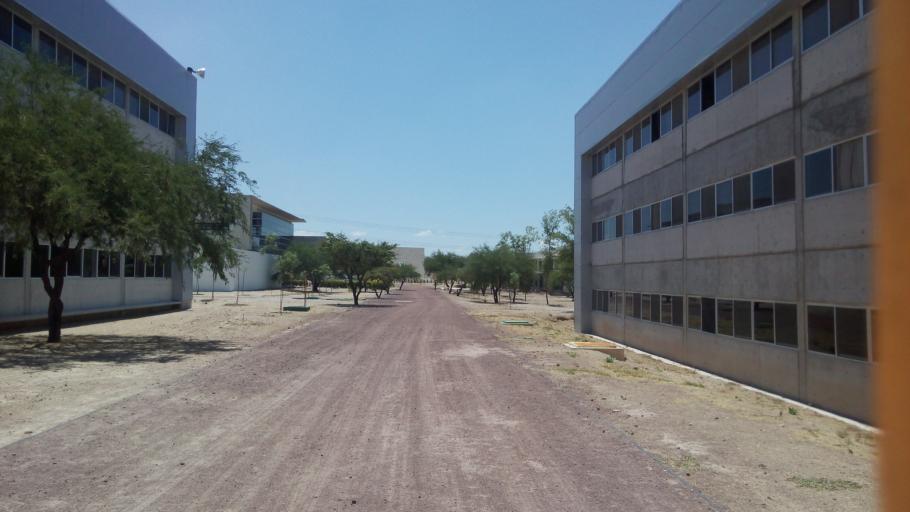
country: MX
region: Aguascalientes
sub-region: Aguascalientes
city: San Sebastian [Fraccionamiento]
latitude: 21.7930
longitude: -102.2906
